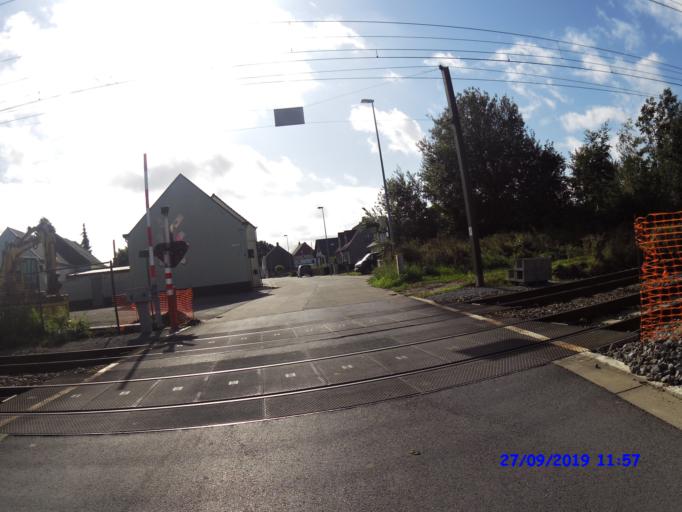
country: BE
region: Flanders
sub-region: Provincie Oost-Vlaanderen
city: Herzele
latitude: 50.8996
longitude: 3.8894
